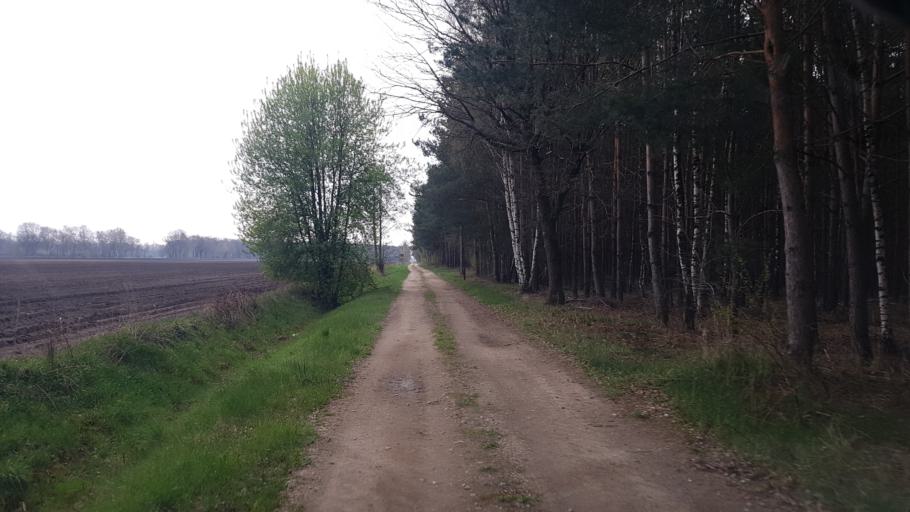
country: DE
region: Brandenburg
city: Bronkow
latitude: 51.6296
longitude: 13.8935
